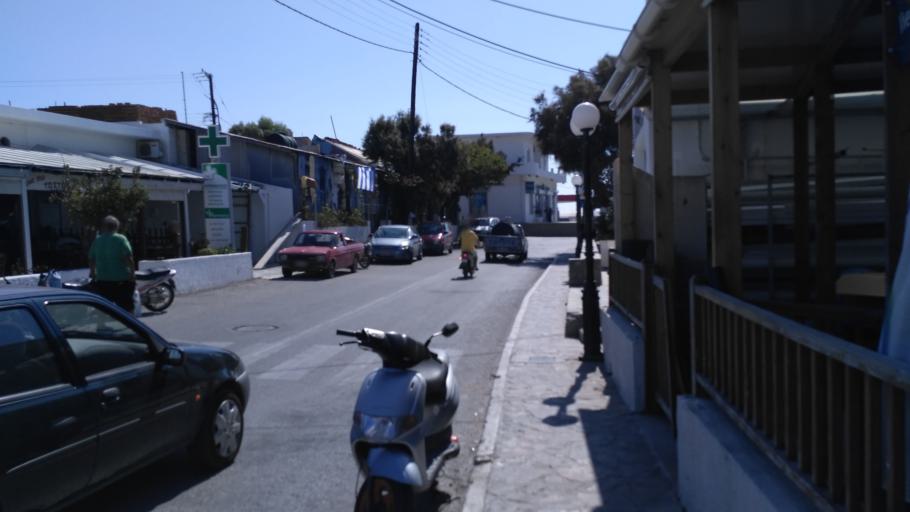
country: GR
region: South Aegean
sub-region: Nomos Kykladon
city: Milos
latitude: 36.7409
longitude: 24.4329
